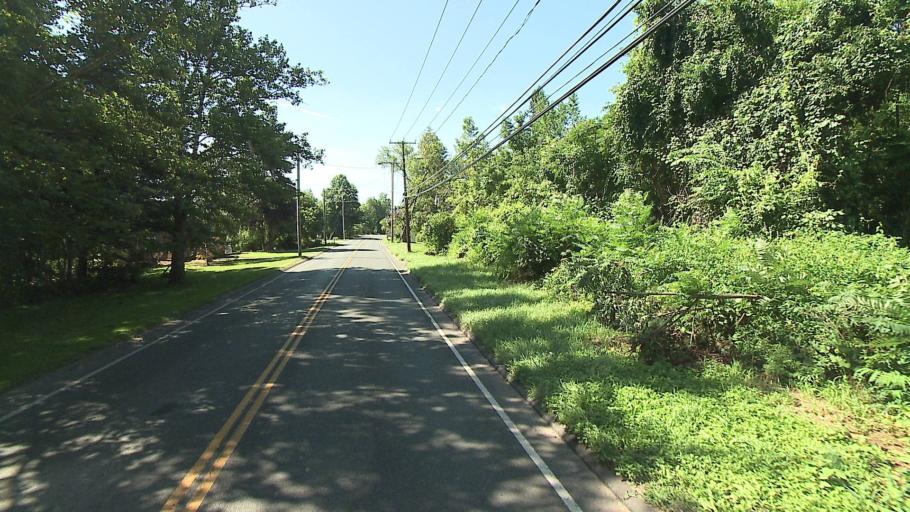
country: US
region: Connecticut
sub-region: Hartford County
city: Tariffville
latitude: 41.9380
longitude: -72.7291
